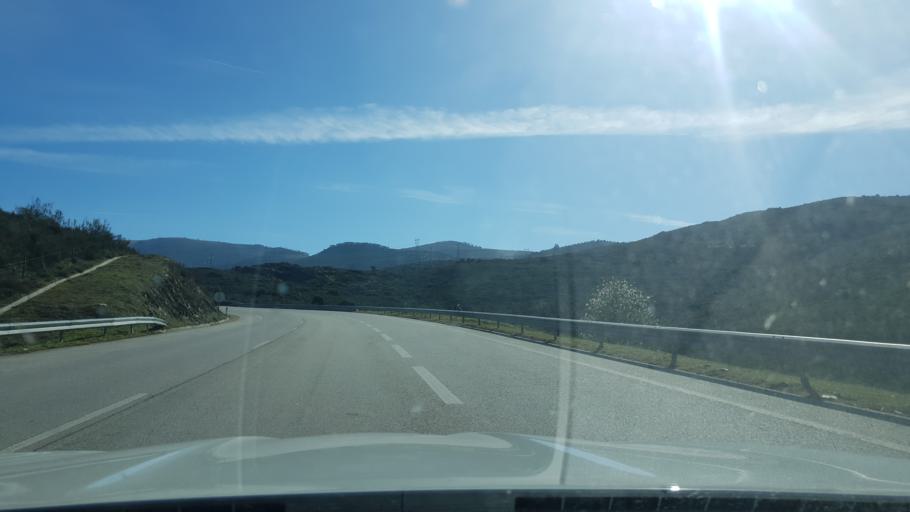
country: PT
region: Braganca
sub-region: Torre de Moncorvo
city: Torre de Moncorvo
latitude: 41.1826
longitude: -7.0892
